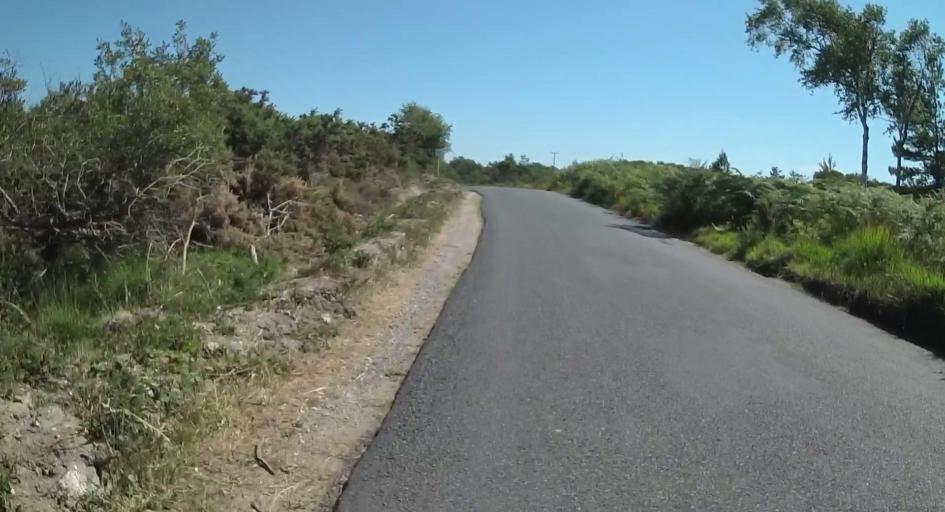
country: GB
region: England
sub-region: Dorset
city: Wareham
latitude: 50.6779
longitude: -2.0674
